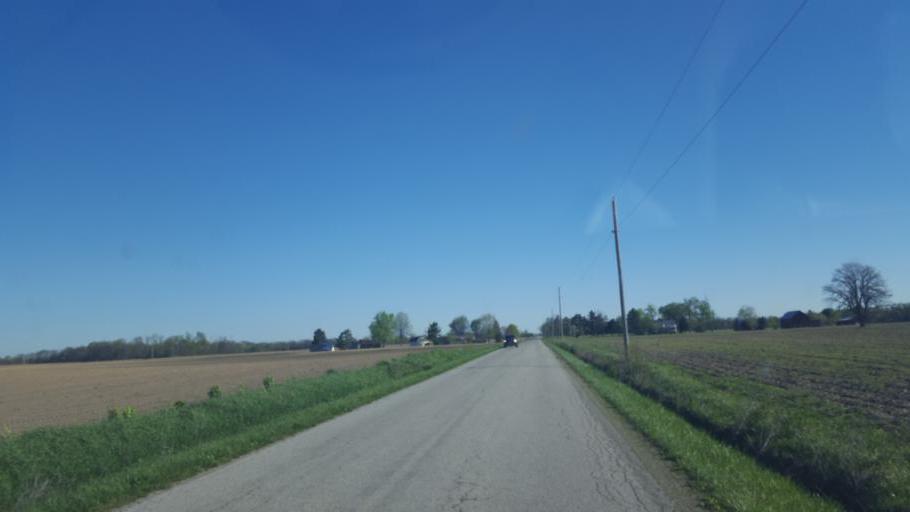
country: US
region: Ohio
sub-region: Morrow County
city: Mount Gilead
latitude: 40.6127
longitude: -82.9184
